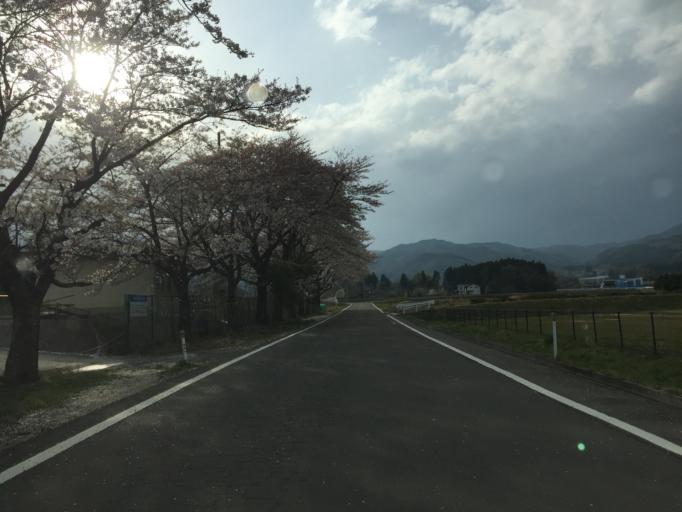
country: JP
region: Fukushima
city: Fukushima-shi
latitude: 37.7621
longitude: 140.3717
